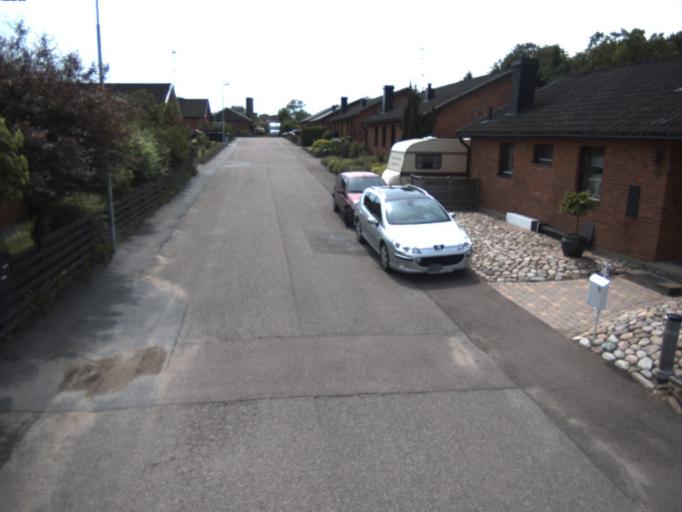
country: SE
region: Skane
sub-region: Helsingborg
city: Odakra
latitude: 56.1087
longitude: 12.7470
